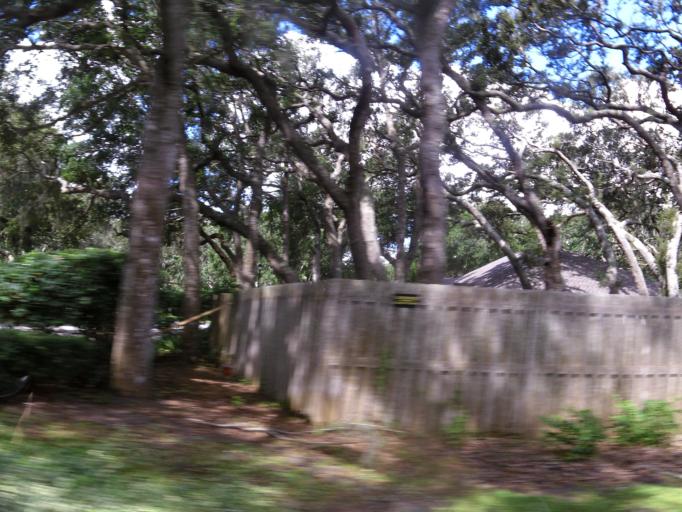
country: US
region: Florida
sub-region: Nassau County
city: Fernandina Beach
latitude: 30.5858
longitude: -81.4464
